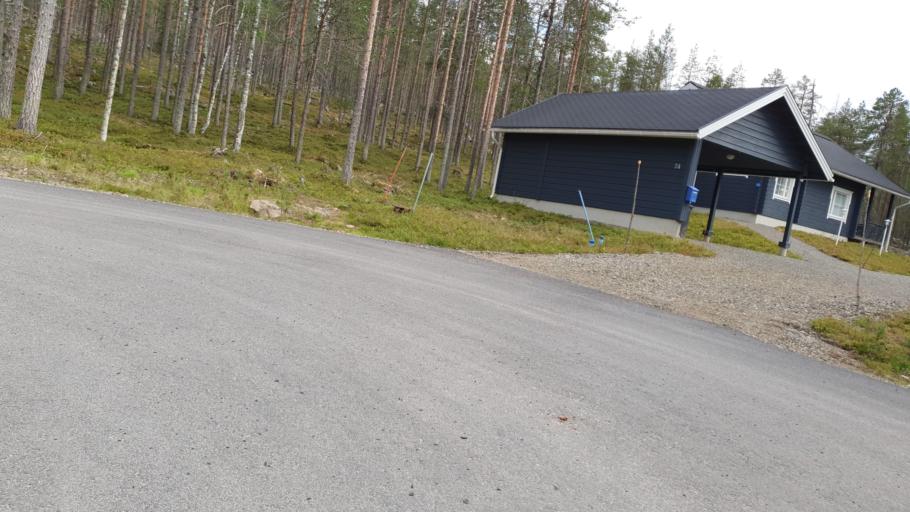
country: FI
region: Lapland
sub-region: Tunturi-Lappi
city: Kolari
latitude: 67.5882
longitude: 24.1174
